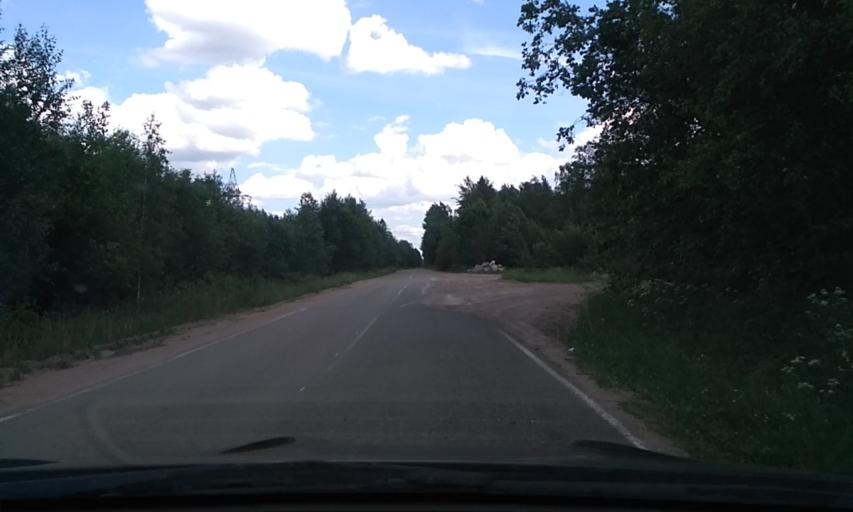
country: RU
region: Leningrad
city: Otradnoye
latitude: 59.8193
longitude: 30.8223
